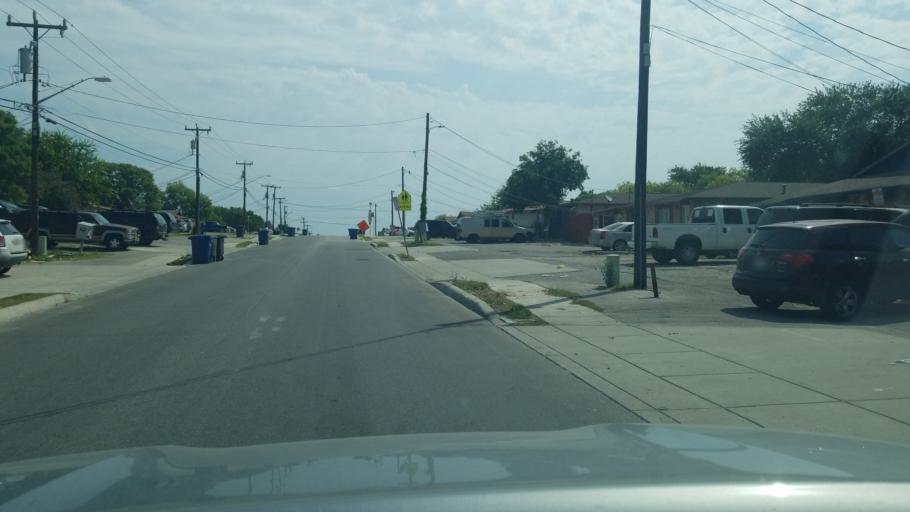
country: US
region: Texas
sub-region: Bexar County
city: Castle Hills
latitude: 29.5416
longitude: -98.5250
